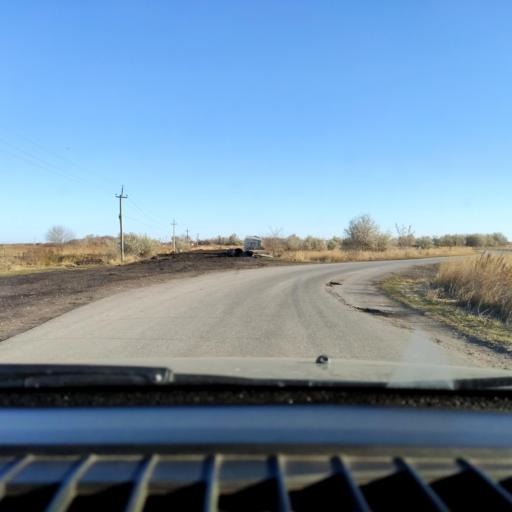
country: RU
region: Samara
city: Tol'yatti
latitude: 53.6552
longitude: 49.3287
